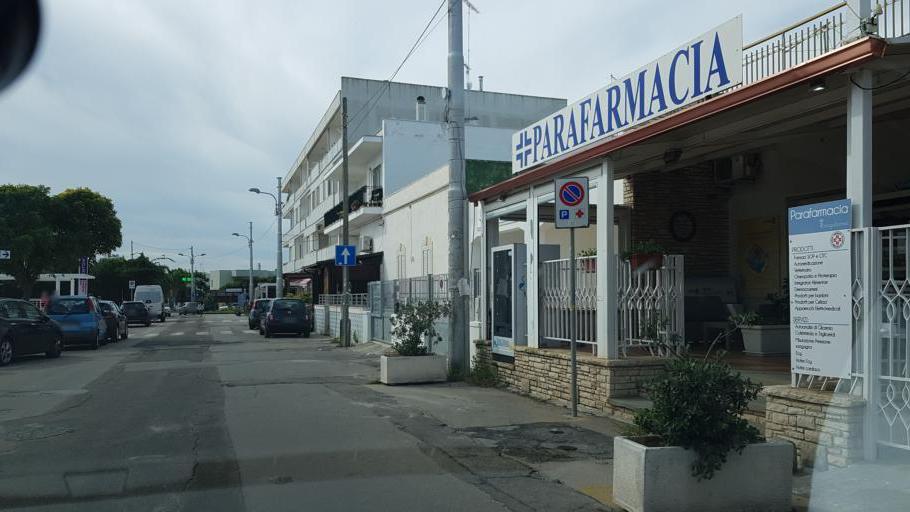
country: IT
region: Apulia
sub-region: Provincia di Lecce
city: Borgagne
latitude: 40.2744
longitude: 18.4284
